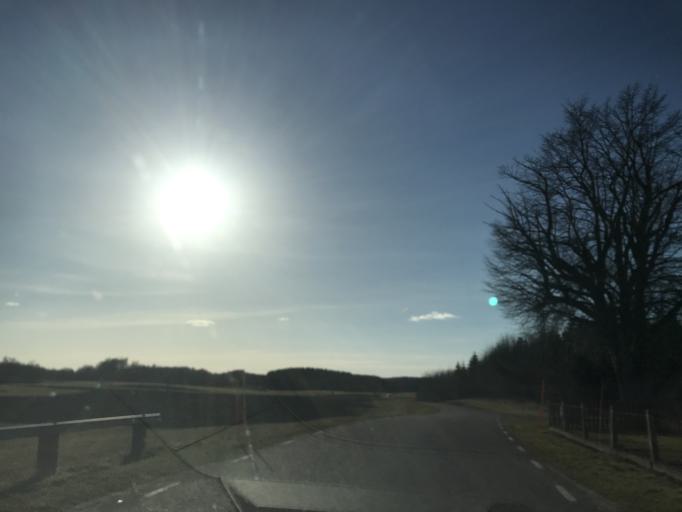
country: SE
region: Skane
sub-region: Ystads Kommun
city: Ystad
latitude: 55.5331
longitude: 13.7790
